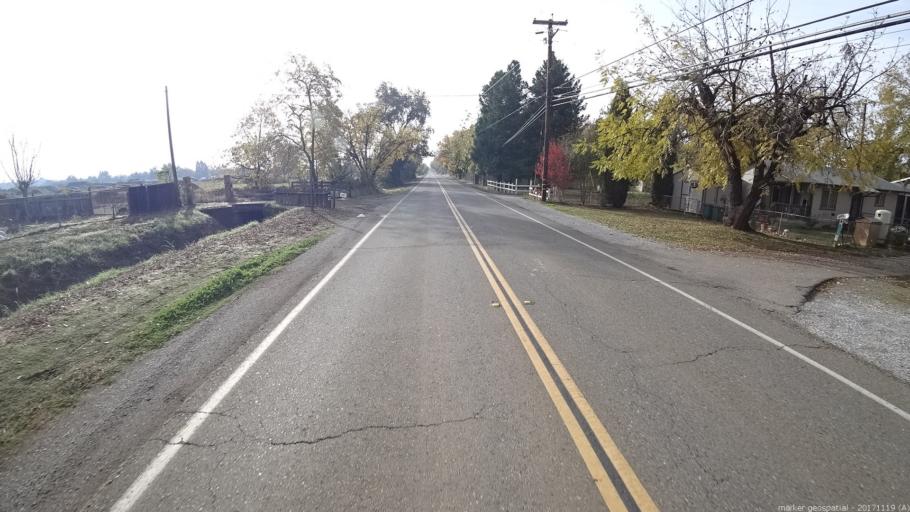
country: US
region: California
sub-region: Shasta County
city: Anderson
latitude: 40.5170
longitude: -122.3337
